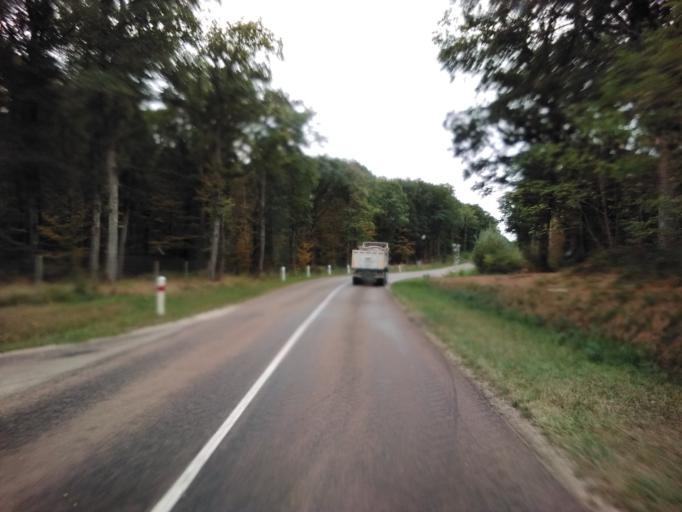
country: FR
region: Champagne-Ardenne
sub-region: Departement de l'Aube
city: Vendeuvre-sur-Barse
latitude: 48.2695
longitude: 4.5047
